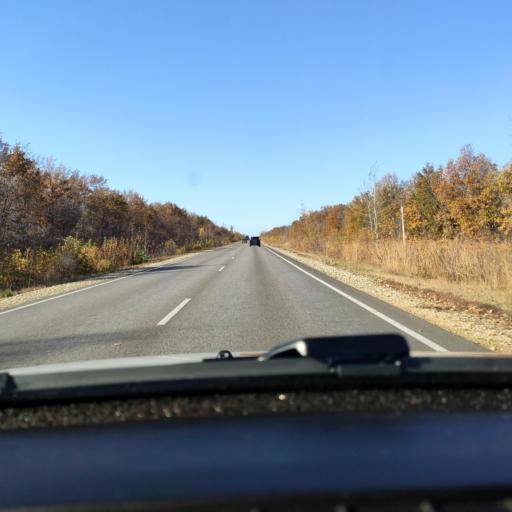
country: RU
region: Voronezj
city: Zemlyansk
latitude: 51.8303
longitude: 38.8266
